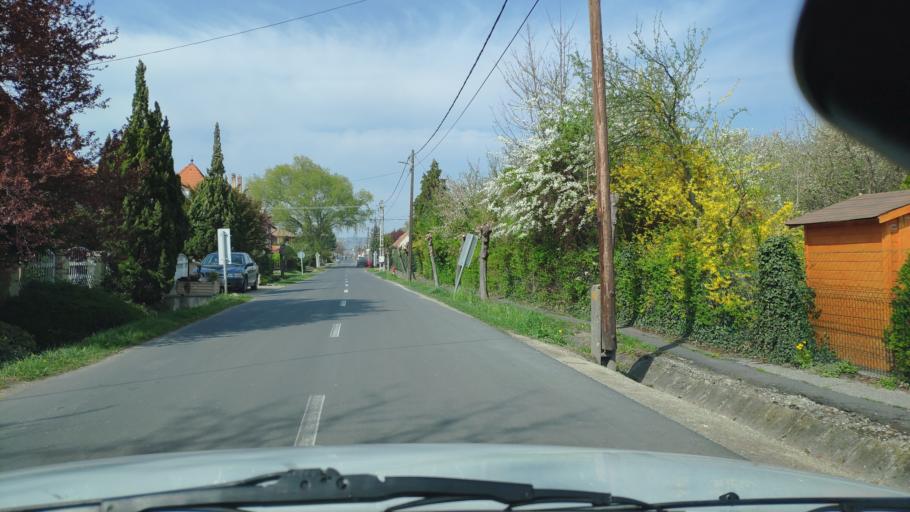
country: HU
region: Zala
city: Keszthely
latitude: 46.7670
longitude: 17.2636
